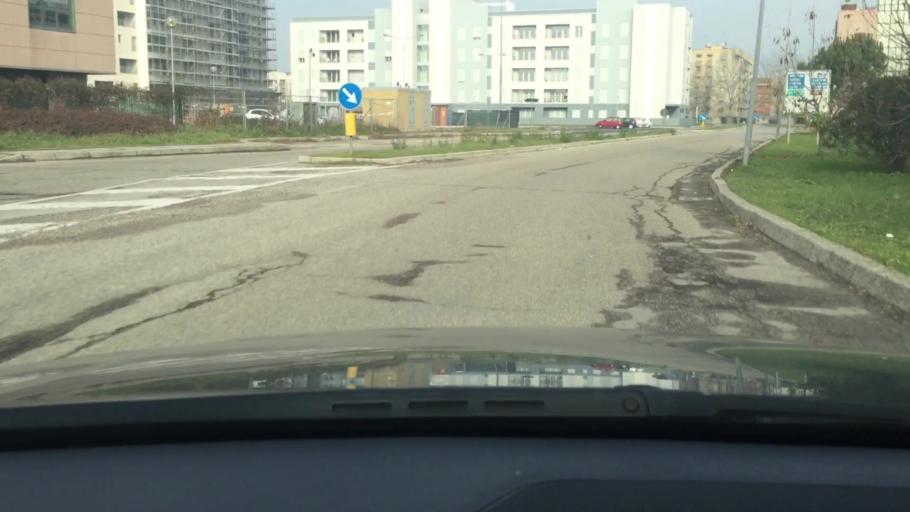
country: IT
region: Emilia-Romagna
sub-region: Provincia di Ferrara
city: Ferrara
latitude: 44.8191
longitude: 11.5966
